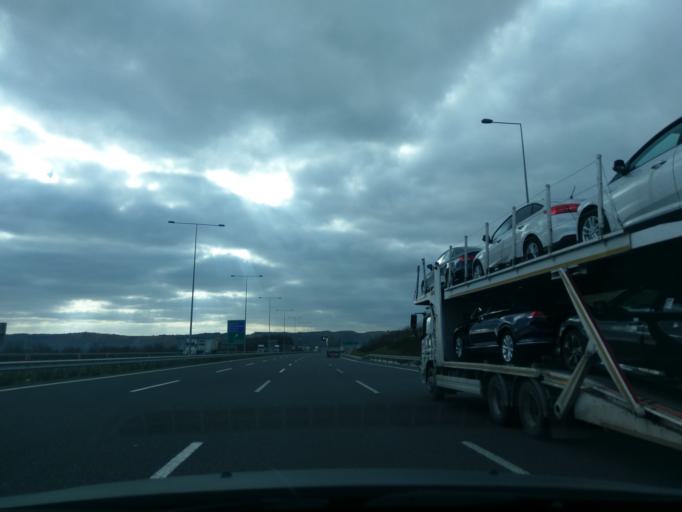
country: TR
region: Istanbul
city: Kemerburgaz
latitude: 41.2235
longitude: 28.8405
